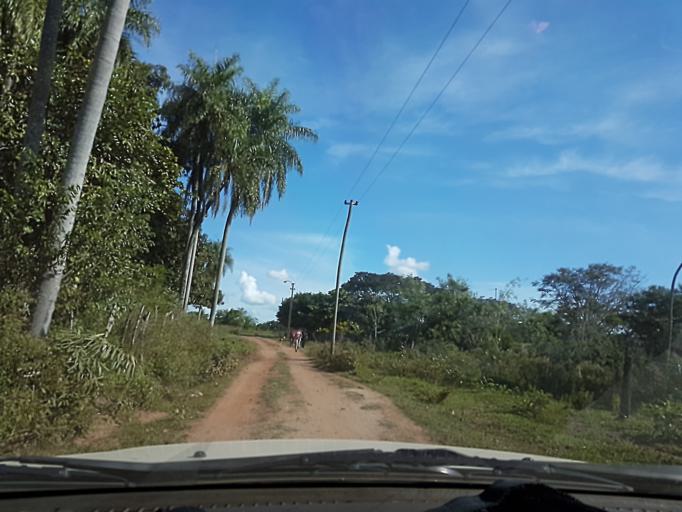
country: PY
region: Cordillera
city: Arroyos y Esteros
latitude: -24.9768
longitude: -57.1947
